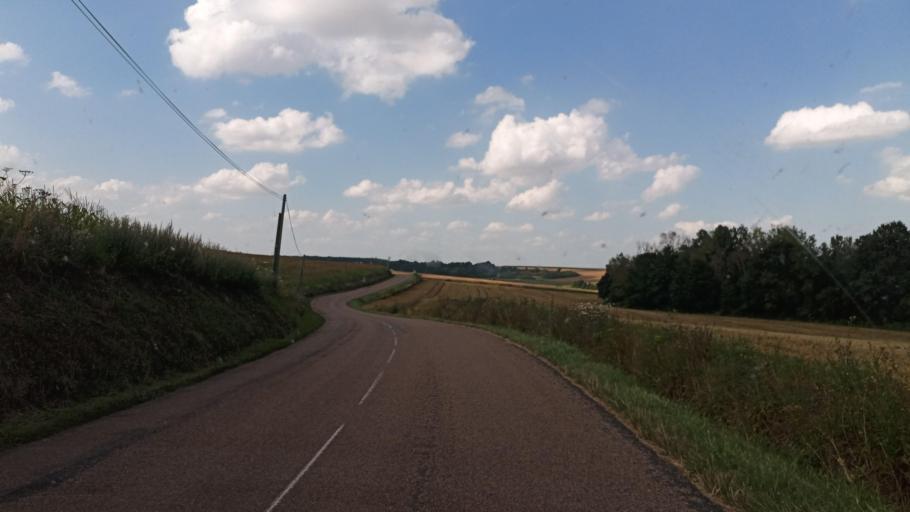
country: FR
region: Bourgogne
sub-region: Departement de l'Yonne
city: Saint-Valerien
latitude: 48.2217
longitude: 3.0662
